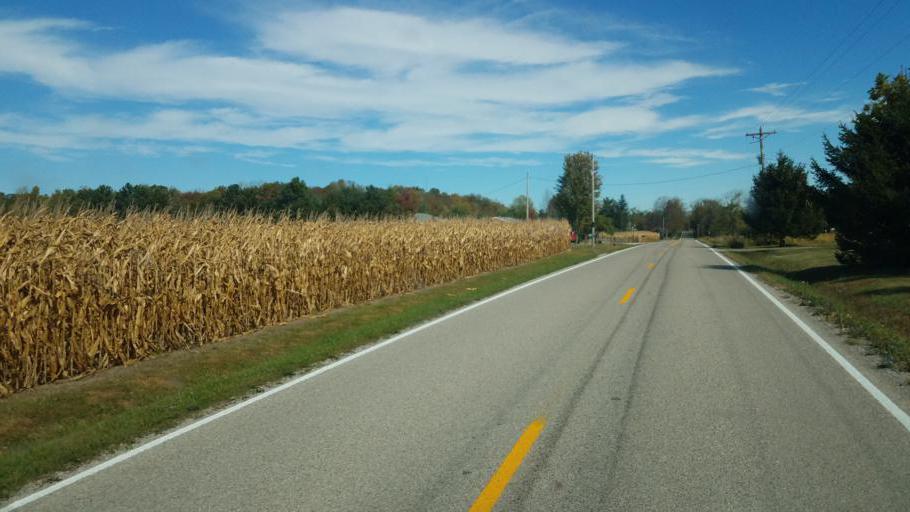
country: US
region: Ohio
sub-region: Huron County
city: New London
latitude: 41.1465
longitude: -82.4658
